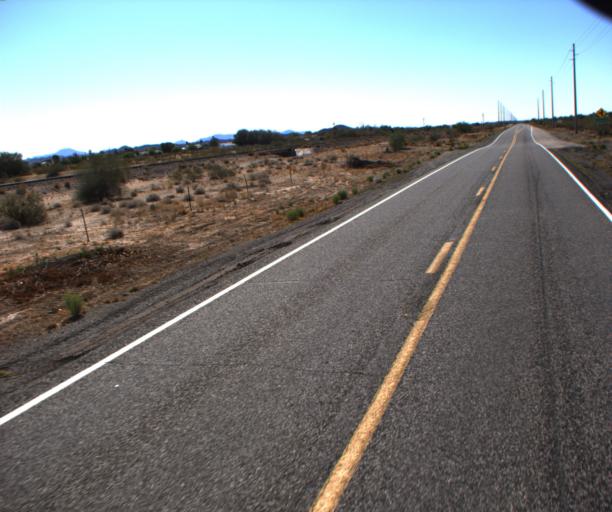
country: US
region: Arizona
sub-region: La Paz County
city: Cienega Springs
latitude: 33.9642
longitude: -114.0354
